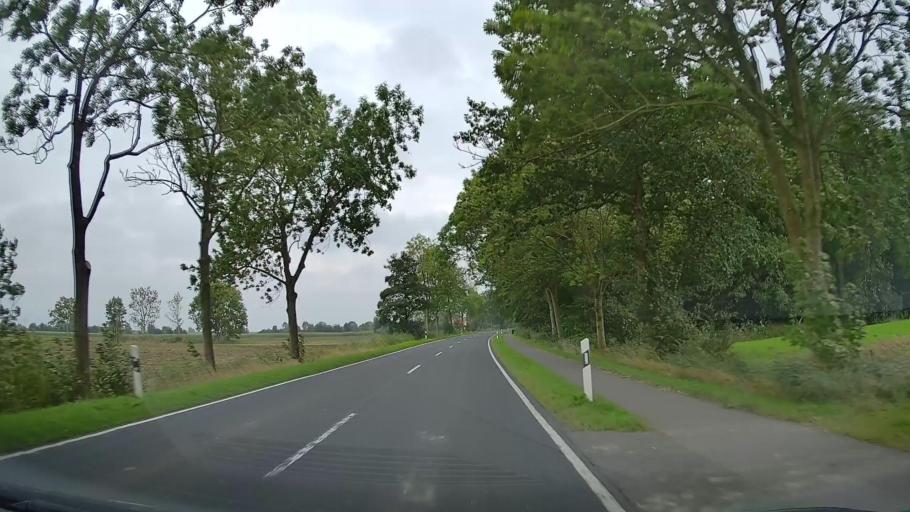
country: DE
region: Lower Saxony
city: Wischhafen
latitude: 53.8014
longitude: 9.3188
